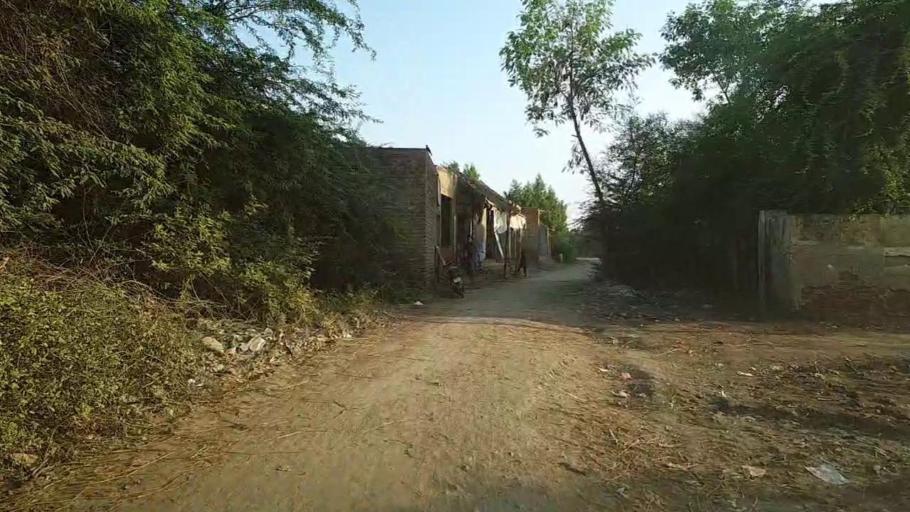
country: PK
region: Sindh
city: Kario
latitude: 24.6890
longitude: 68.6731
